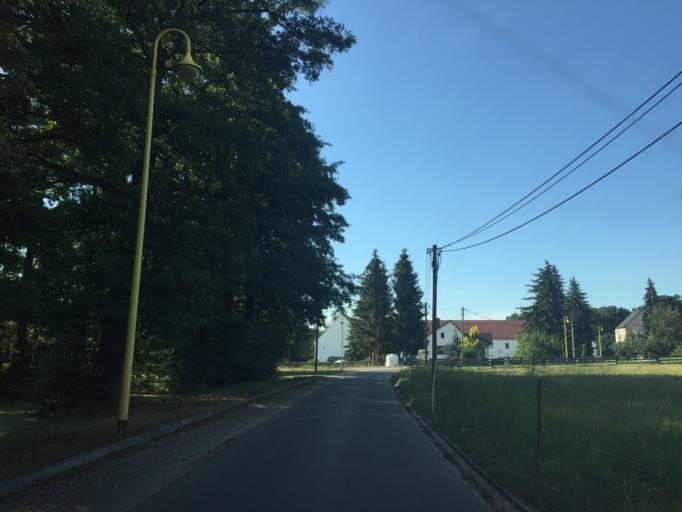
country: DE
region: Thuringia
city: Heyersdorf
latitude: 50.8649
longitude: 12.3323
